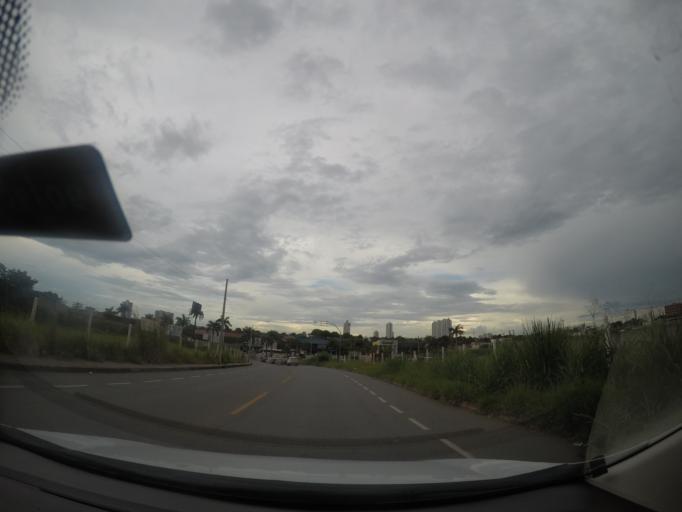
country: BR
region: Goias
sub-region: Goiania
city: Goiania
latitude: -16.6535
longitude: -49.2646
